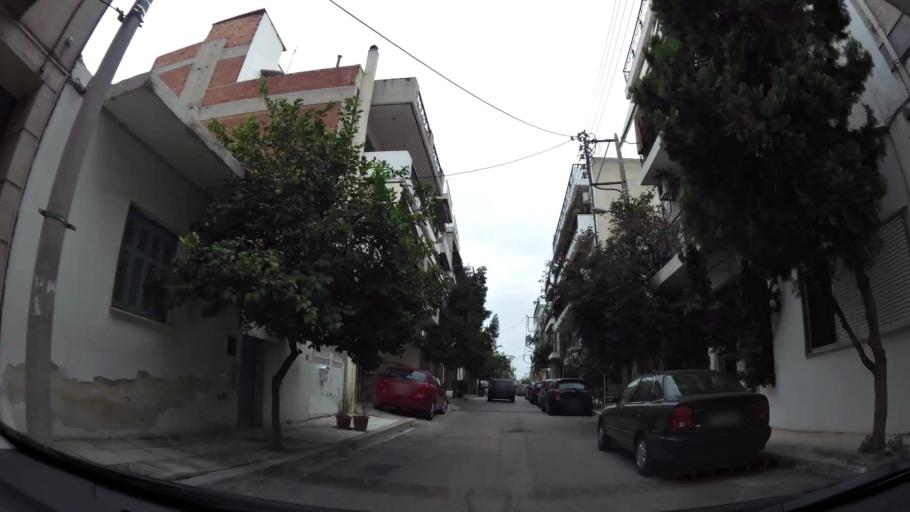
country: GR
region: Attica
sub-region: Nomarchia Athinas
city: Peristeri
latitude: 37.9995
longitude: 23.6870
